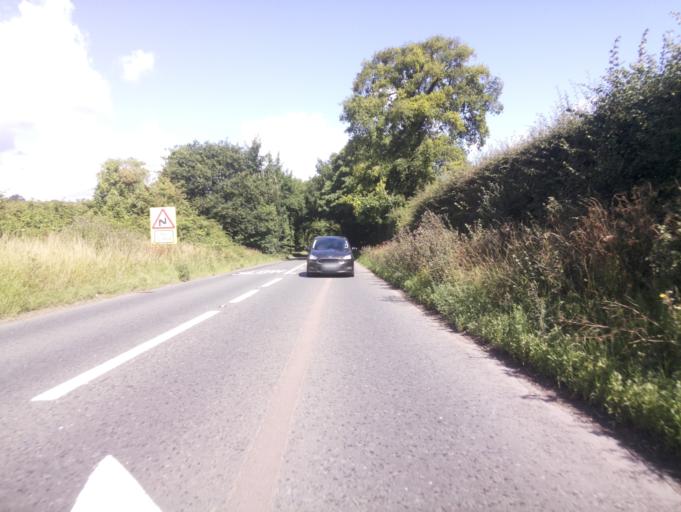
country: GB
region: England
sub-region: Gloucestershire
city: Gloucester
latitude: 51.8824
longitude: -2.3101
